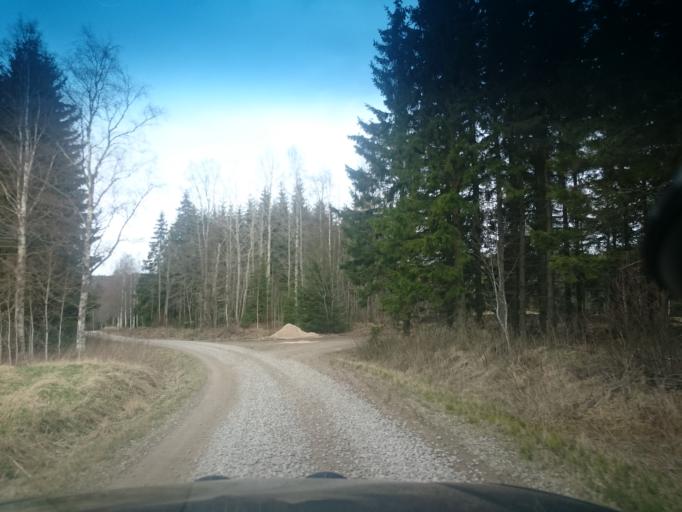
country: SE
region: Joenkoeping
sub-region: Vetlanda Kommun
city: Vetlanda
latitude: 57.3354
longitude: 15.1580
